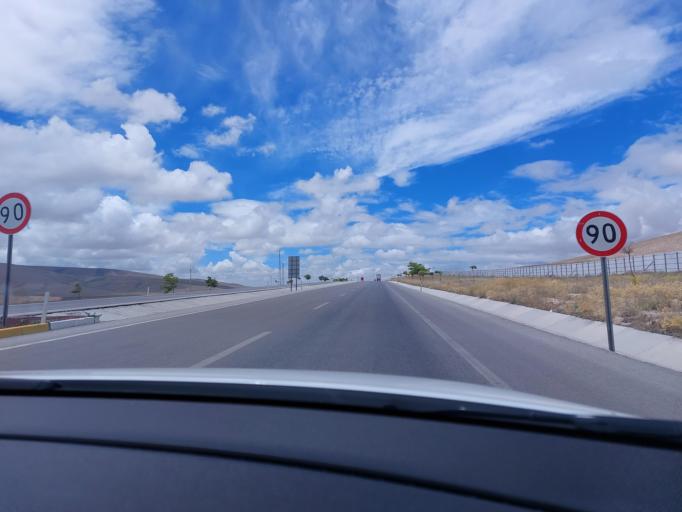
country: TR
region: Konya
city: Obruk
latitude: 38.0612
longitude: 33.0420
